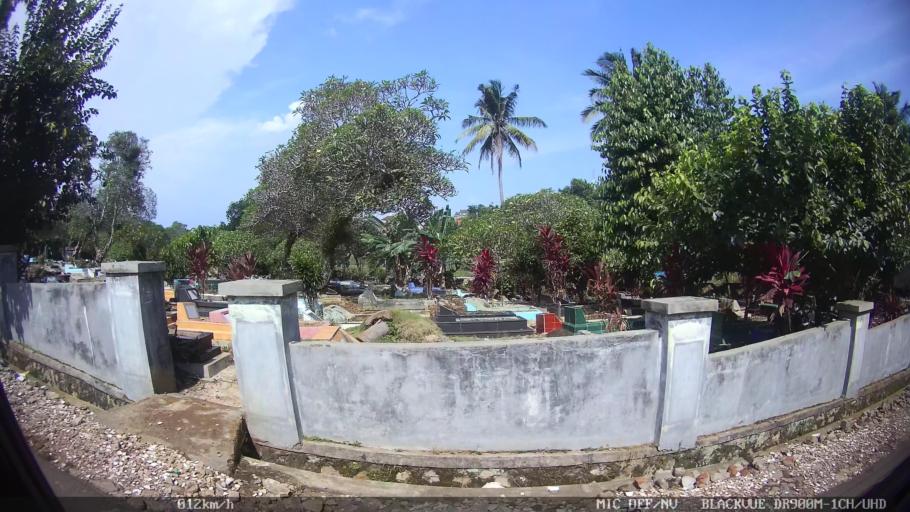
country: ID
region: Lampung
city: Kedaton
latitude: -5.3973
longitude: 105.2437
